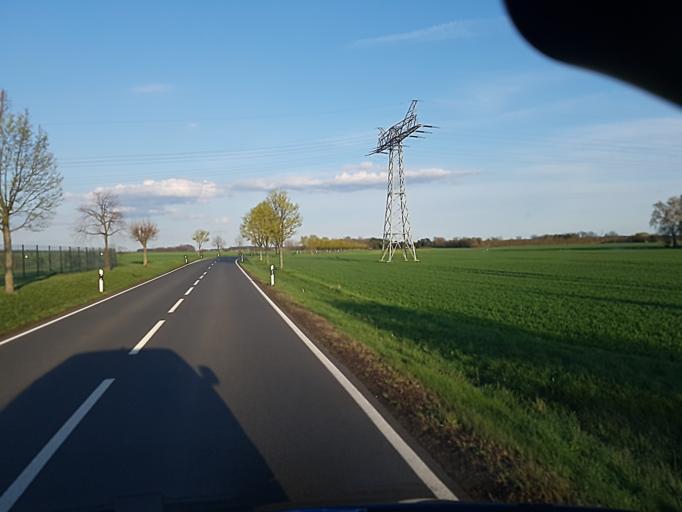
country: DE
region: Saxony
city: Bad Duben
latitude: 51.5898
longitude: 12.6075
